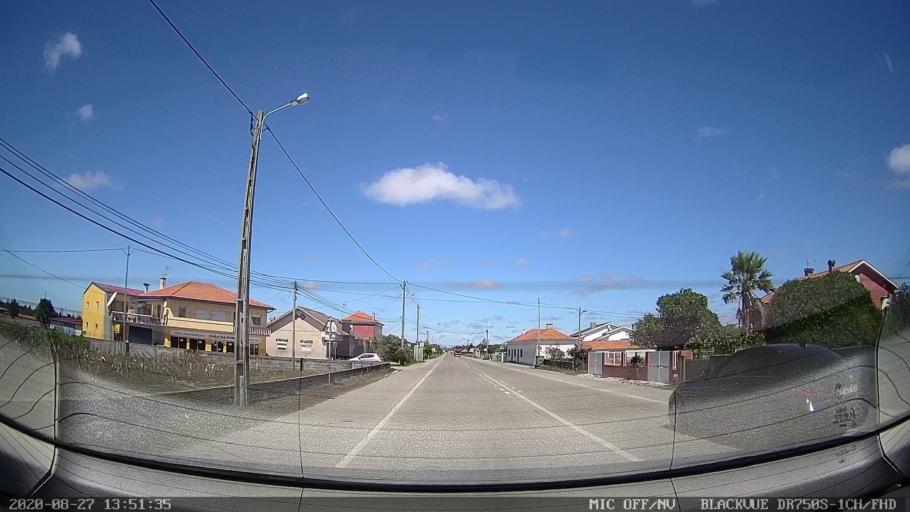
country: PT
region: Coimbra
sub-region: Mira
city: Mira
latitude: 40.3468
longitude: -8.7491
